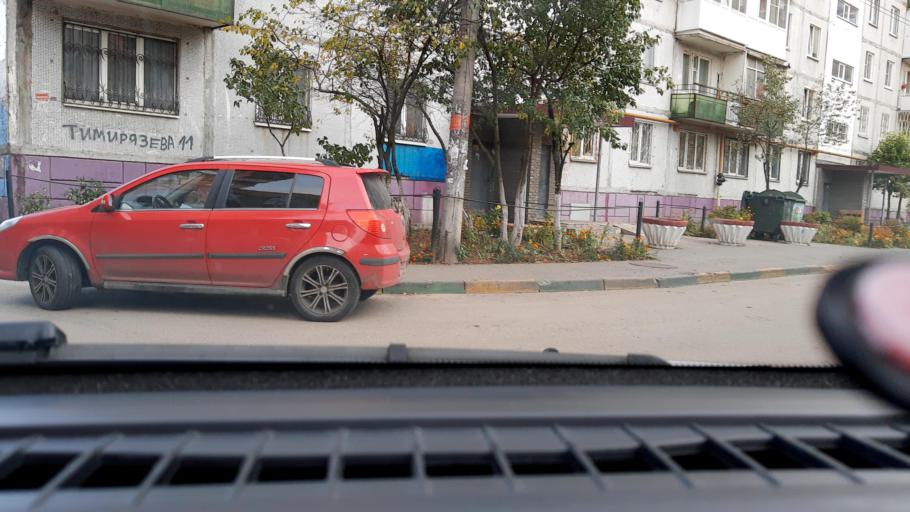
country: RU
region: Nizjnij Novgorod
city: Nizhniy Novgorod
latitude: 56.3068
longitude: 44.0003
